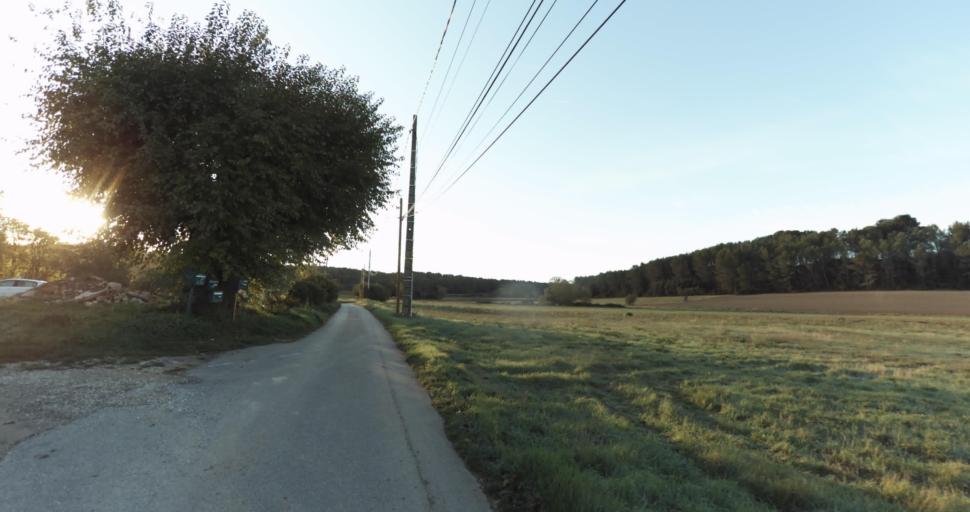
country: FR
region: Provence-Alpes-Cote d'Azur
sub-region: Departement des Bouches-du-Rhone
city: Venelles
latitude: 43.5780
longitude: 5.5004
